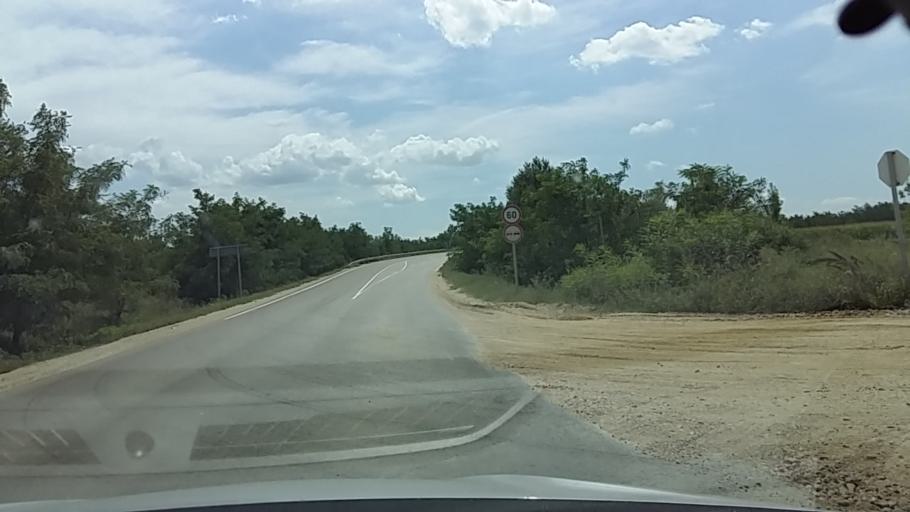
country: HU
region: Borsod-Abauj-Zemplen
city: Hejobaba
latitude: 47.8832
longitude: 20.8989
